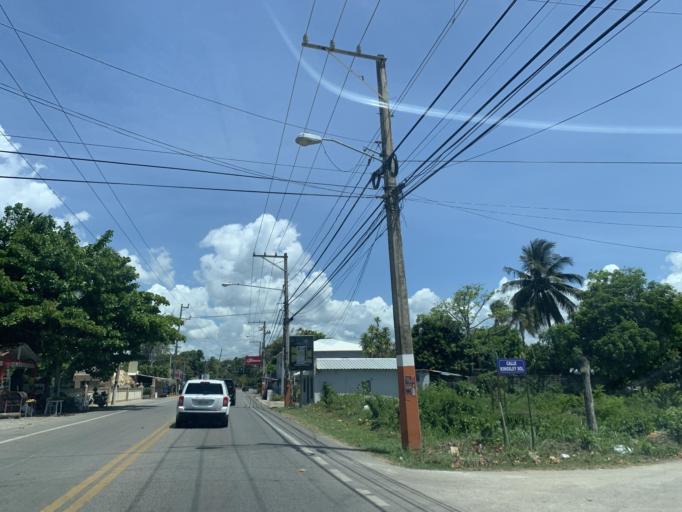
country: DO
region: Puerto Plata
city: Cabarete
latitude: 19.7356
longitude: -70.3896
